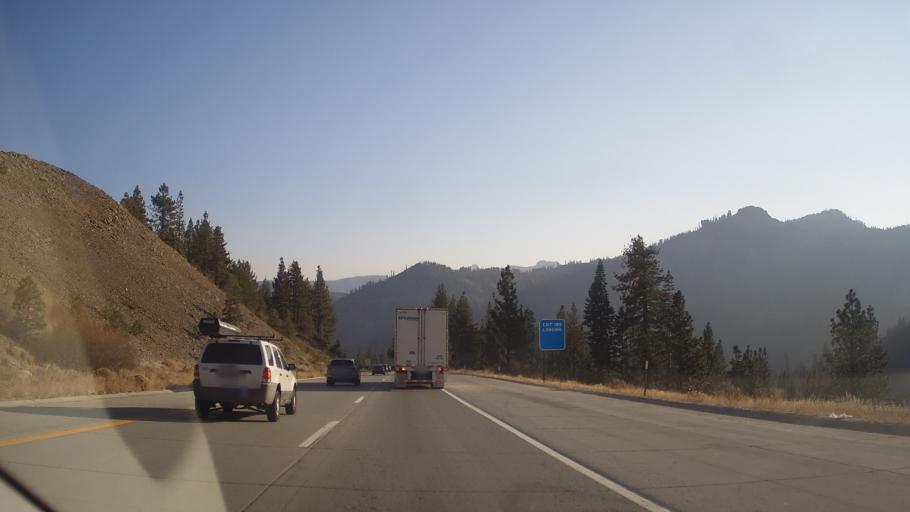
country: US
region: California
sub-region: Nevada County
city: Truckee
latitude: 39.3360
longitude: -120.3068
